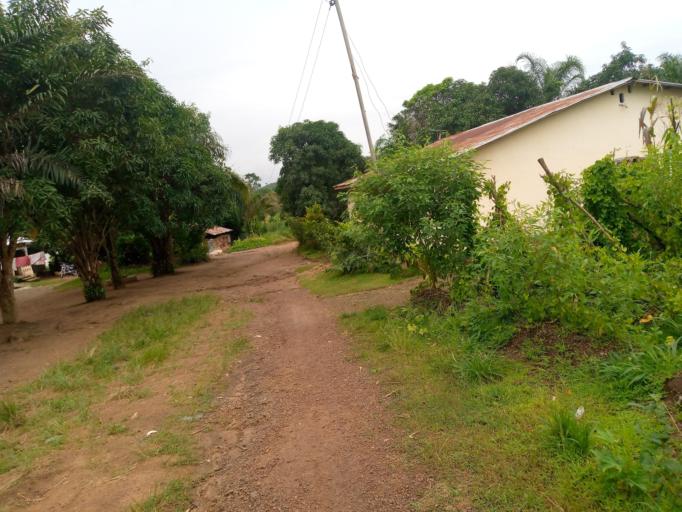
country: SL
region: Eastern Province
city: Kenema
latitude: 7.8426
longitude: -11.2021
